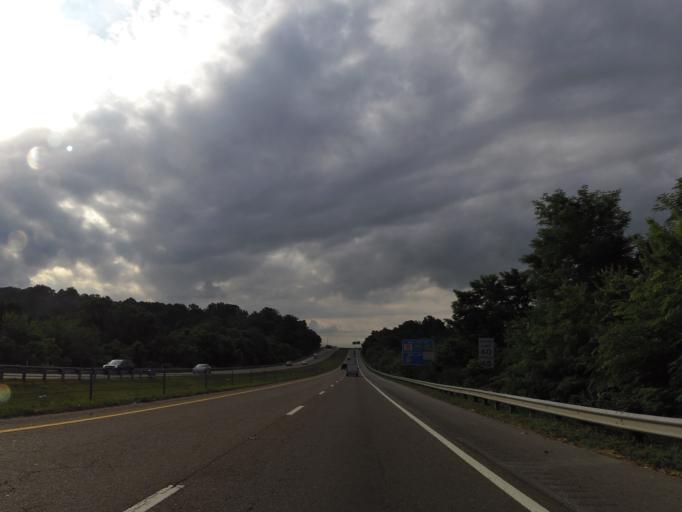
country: US
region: Tennessee
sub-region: Blount County
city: Alcoa
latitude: 35.8407
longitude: -83.9814
